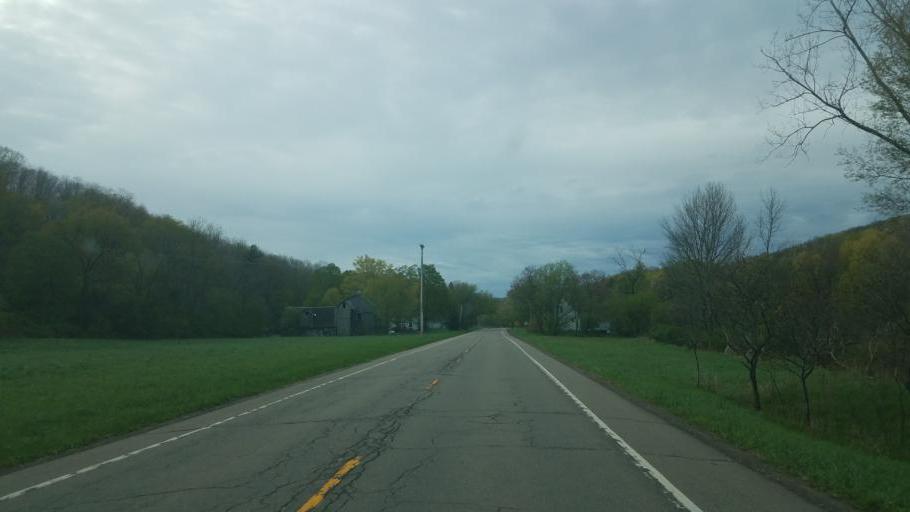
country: US
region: New York
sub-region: Steuben County
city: Canisteo
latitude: 42.2076
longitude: -77.5619
